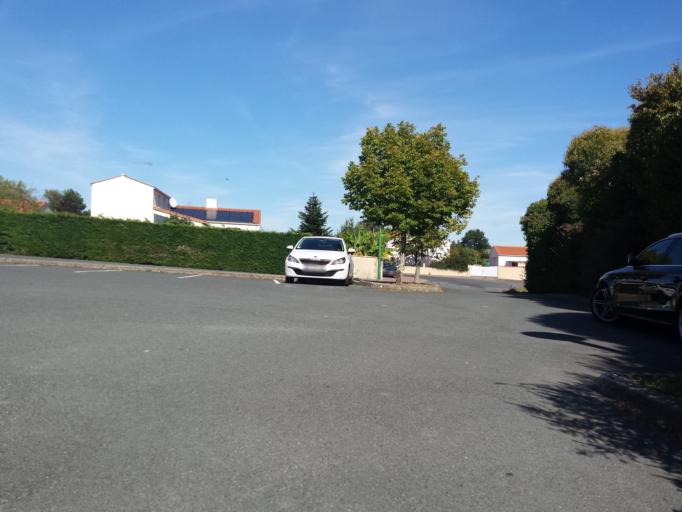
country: FR
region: Pays de la Loire
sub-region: Departement de la Vendee
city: La Chaize-le-Vicomte
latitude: 46.6723
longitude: -1.2886
